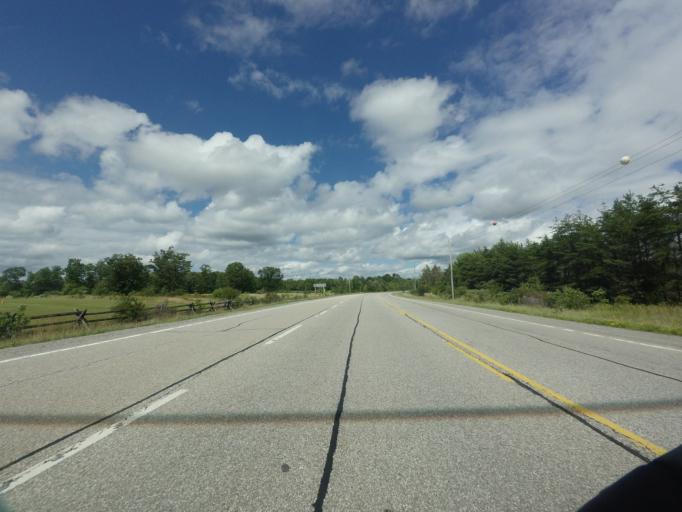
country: CA
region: Ontario
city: Perth
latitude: 44.7370
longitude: -76.1437
